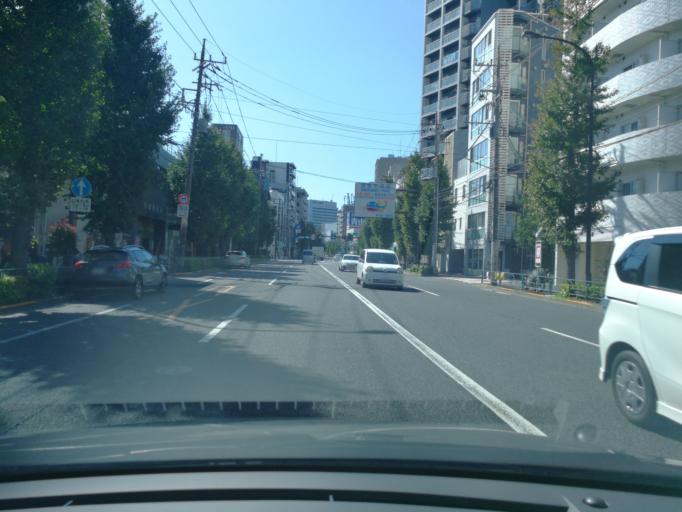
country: JP
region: Tokyo
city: Tokyo
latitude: 35.6133
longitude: 139.7074
